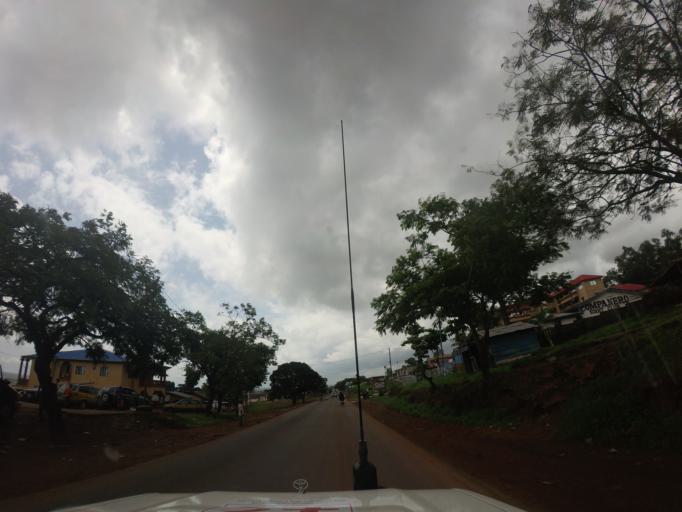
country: SL
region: Western Area
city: Hastings
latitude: 8.3799
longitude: -13.1055
